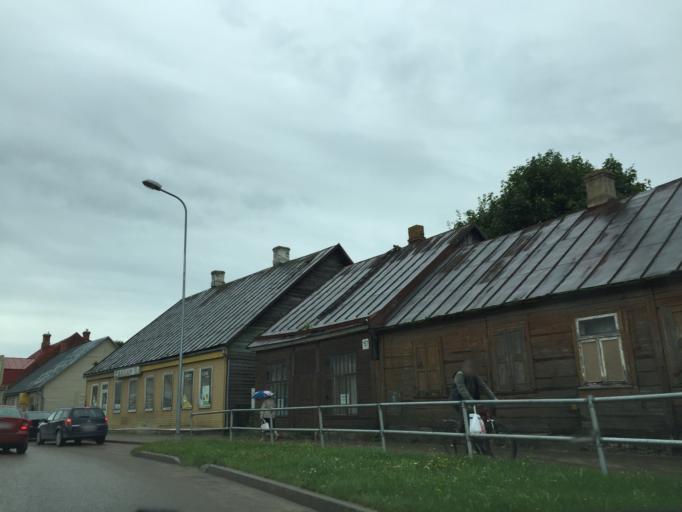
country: LV
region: Jekabpils Rajons
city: Jekabpils
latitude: 56.5028
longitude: 25.8675
